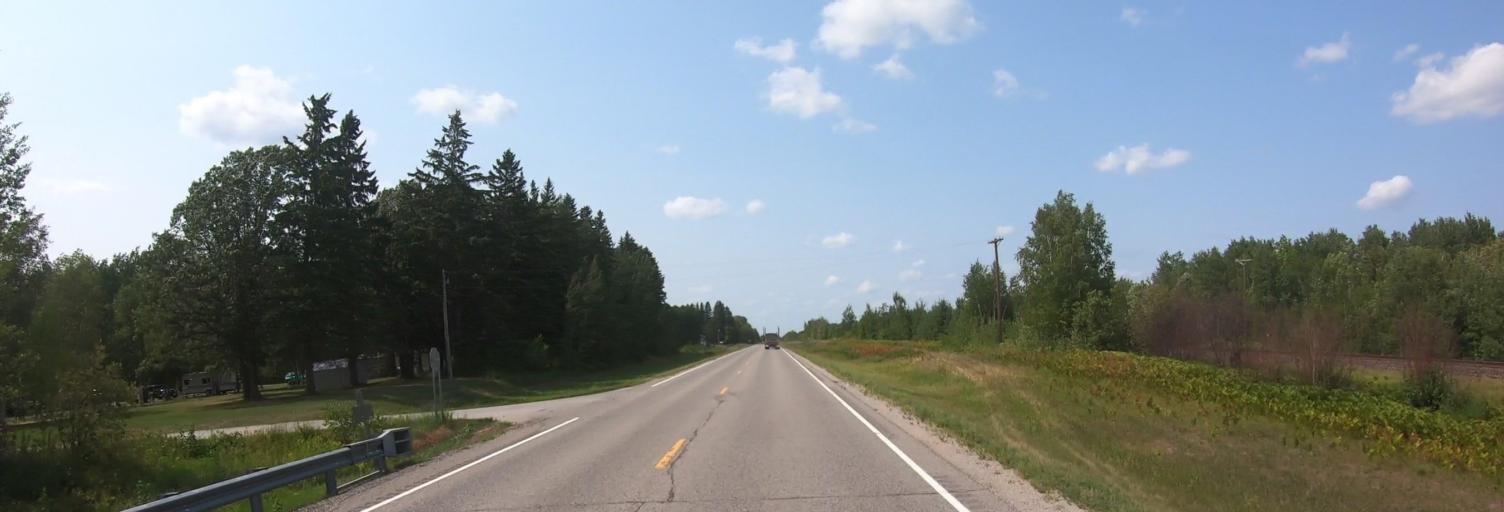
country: US
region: Minnesota
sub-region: Roseau County
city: Warroad
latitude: 48.8097
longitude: -95.1154
